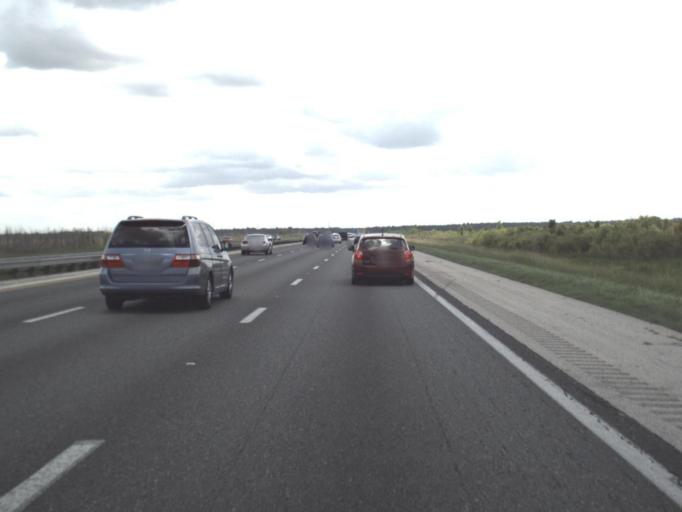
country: US
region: Florida
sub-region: Alachua County
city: Gainesville
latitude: 29.5822
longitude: -82.3581
